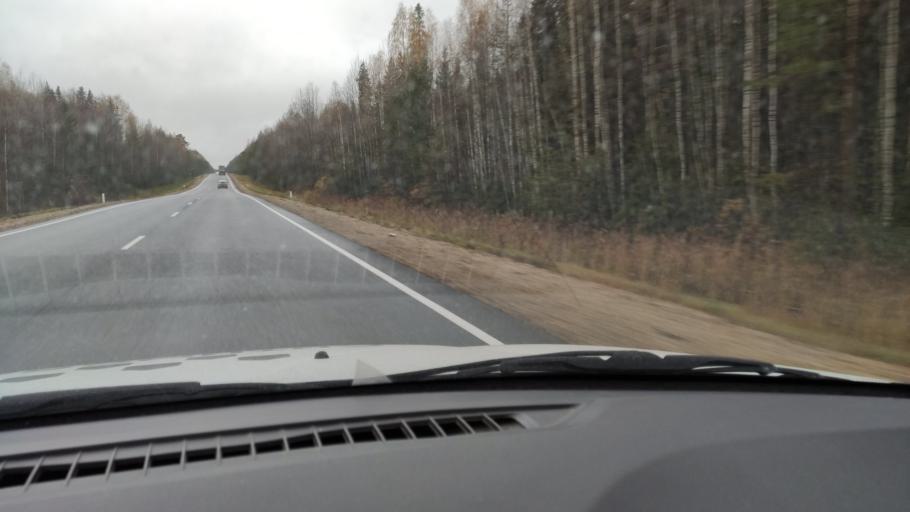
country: RU
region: Kirov
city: Chernaya Kholunitsa
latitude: 58.8590
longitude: 51.6738
